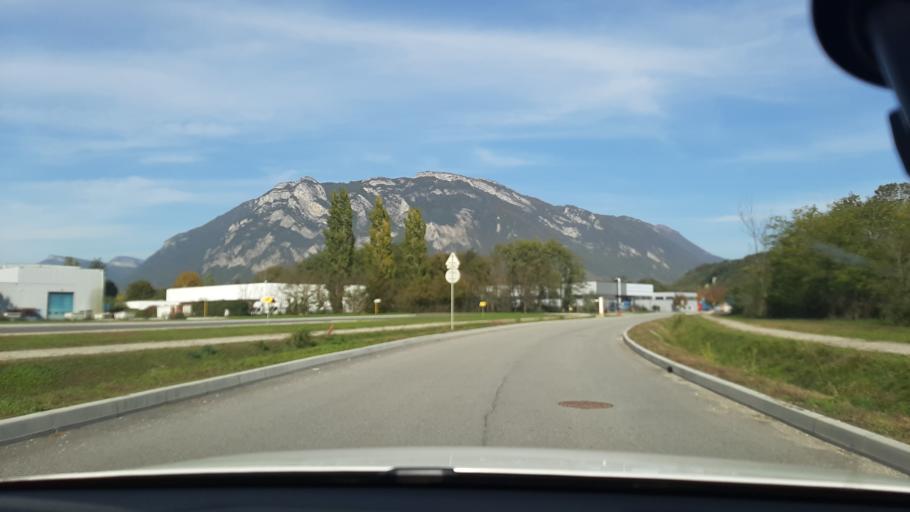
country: FR
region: Rhone-Alpes
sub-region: Departement de la Savoie
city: Montmelian
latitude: 45.4743
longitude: 6.0354
